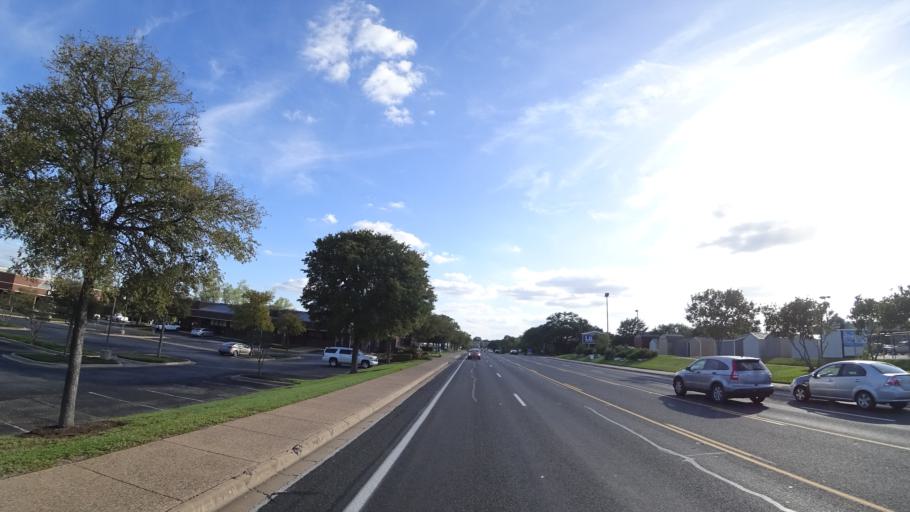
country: US
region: Texas
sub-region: Williamson County
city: Jollyville
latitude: 30.3641
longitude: -97.7395
